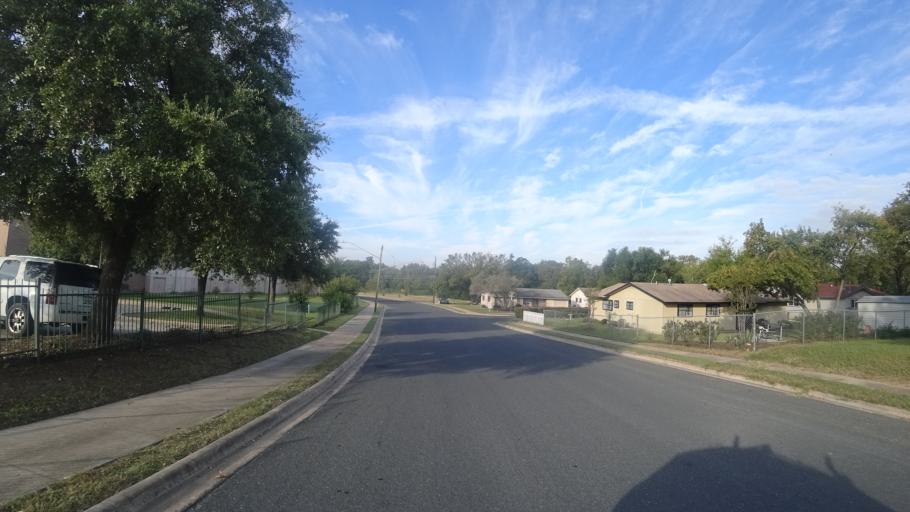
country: US
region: Texas
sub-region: Travis County
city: Austin
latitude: 30.2728
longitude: -97.7105
